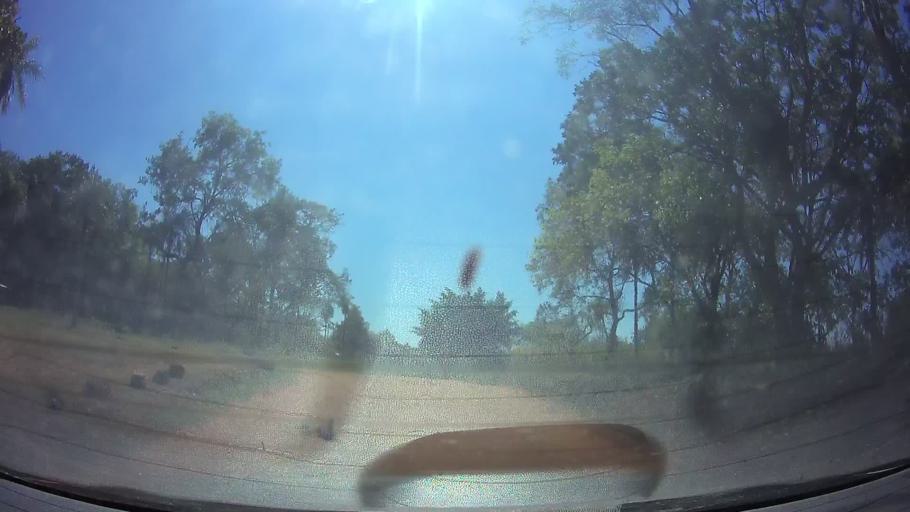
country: PY
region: Central
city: Limpio
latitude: -25.2407
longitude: -57.4430
